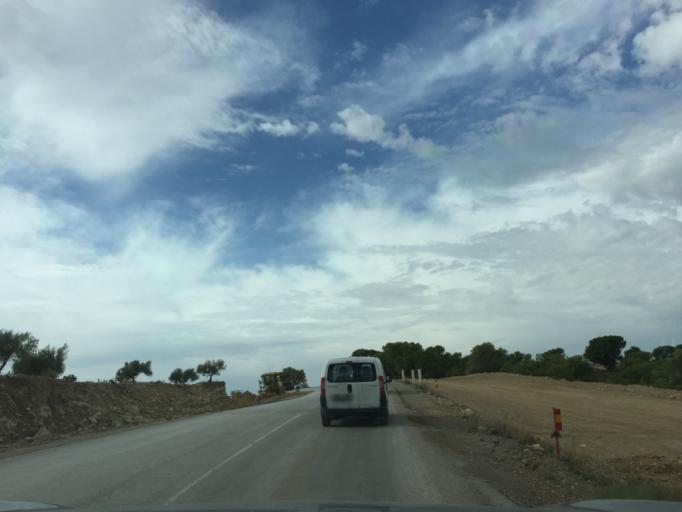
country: TN
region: Zaghwan
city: El Fahs
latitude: 36.2924
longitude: 9.8093
